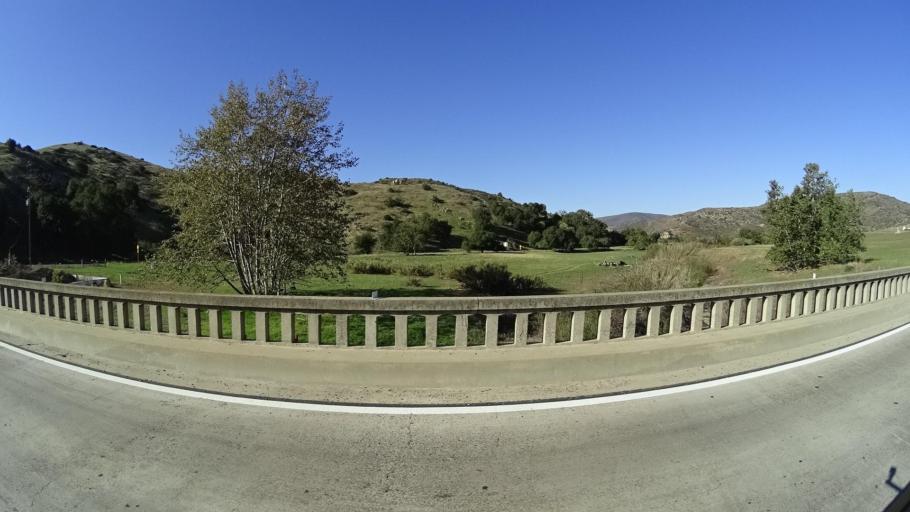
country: US
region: California
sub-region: San Diego County
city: Jamul
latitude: 32.6687
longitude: -116.8241
